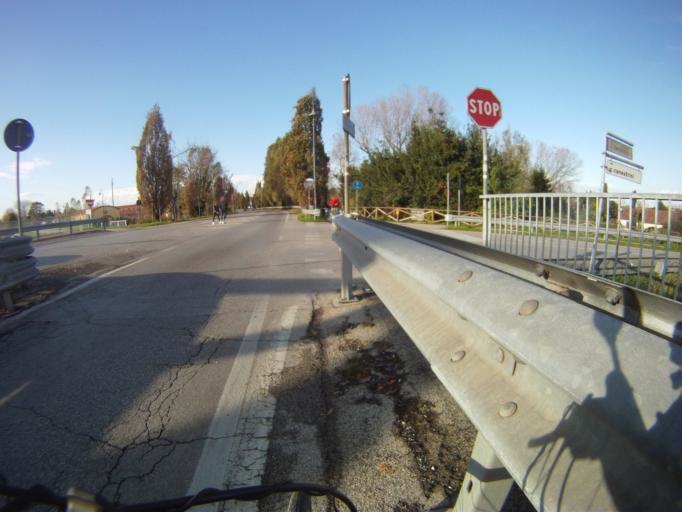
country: IT
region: Veneto
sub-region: Provincia di Padova
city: Padova
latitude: 45.3842
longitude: 11.8996
